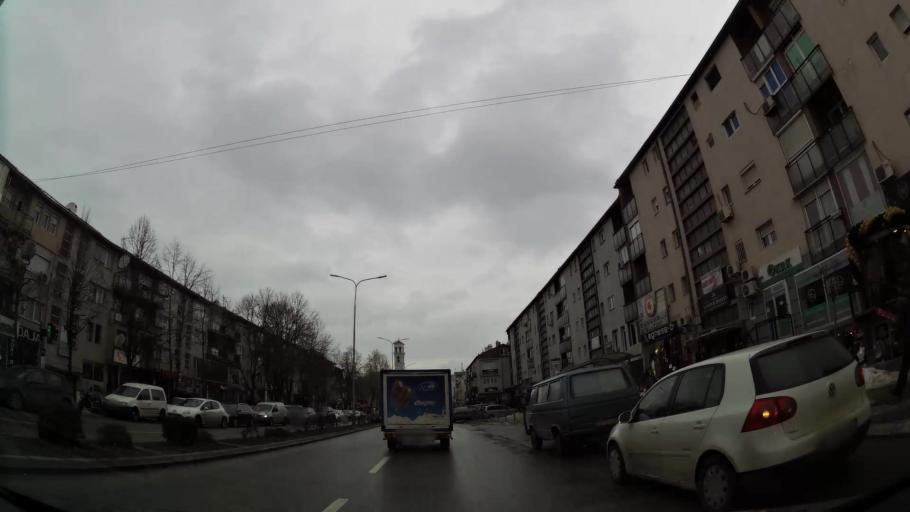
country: XK
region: Pristina
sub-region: Komuna e Prishtines
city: Pristina
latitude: 42.6526
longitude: 21.1589
